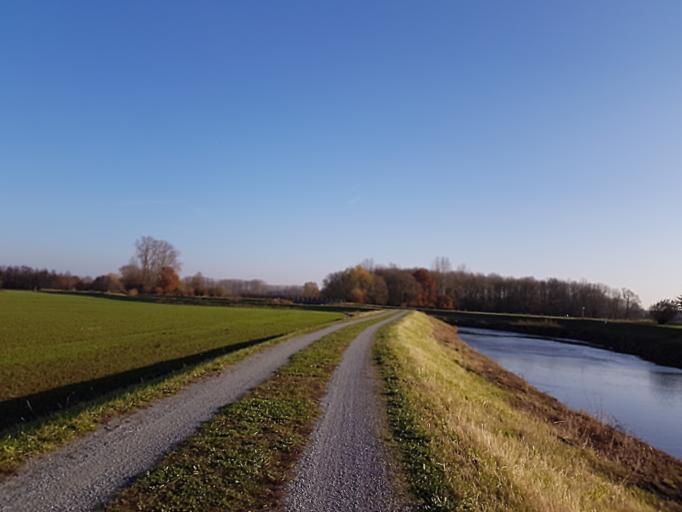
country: BE
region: Flanders
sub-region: Provincie Antwerpen
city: Bonheiden
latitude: 51.0013
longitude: 4.5593
